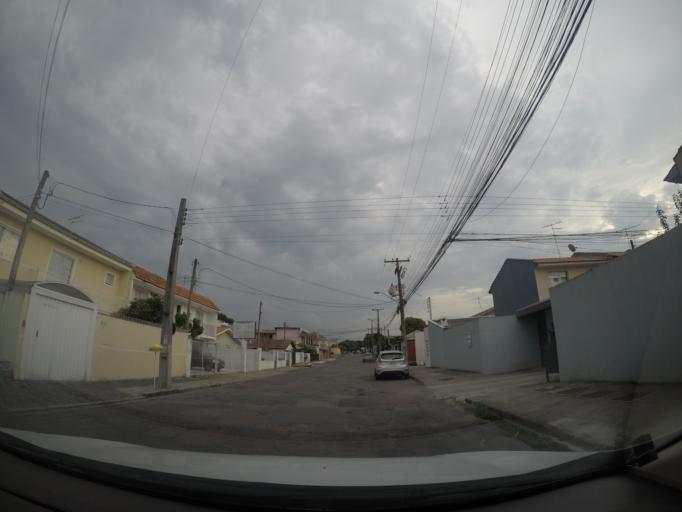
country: BR
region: Parana
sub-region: Sao Jose Dos Pinhais
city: Sao Jose dos Pinhais
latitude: -25.5211
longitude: -49.2337
